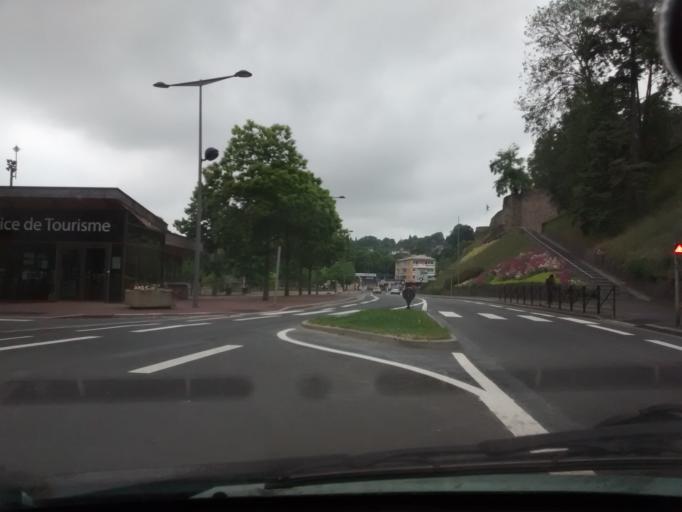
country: FR
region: Lower Normandy
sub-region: Departement de la Manche
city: Saint-Lo
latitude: 49.1151
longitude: -1.0982
